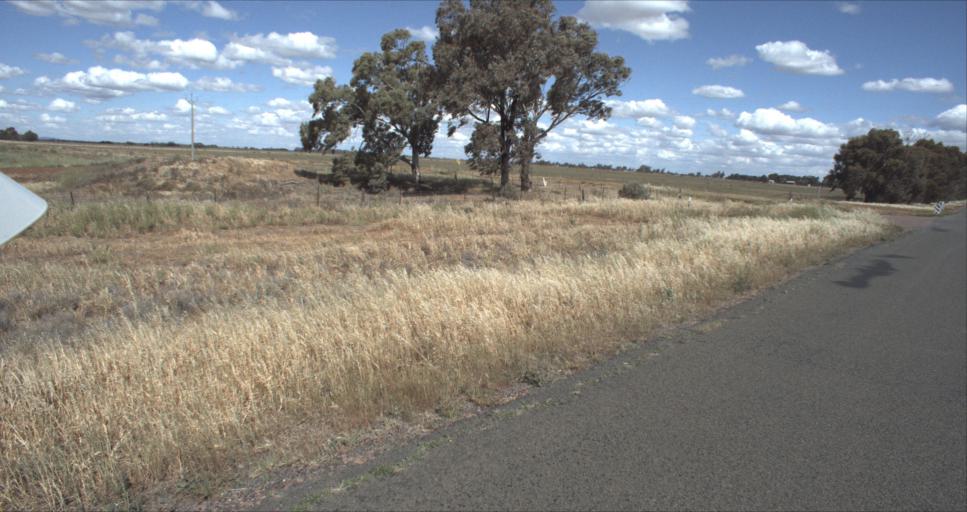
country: AU
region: New South Wales
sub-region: Leeton
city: Leeton
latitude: -34.4706
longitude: 146.2510
